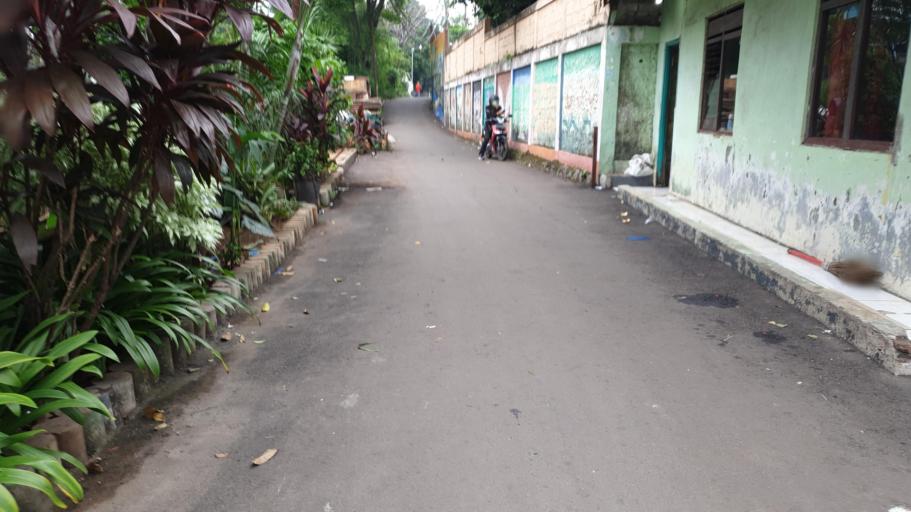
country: ID
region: Banten
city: South Tangerang
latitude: -6.2610
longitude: 106.7830
